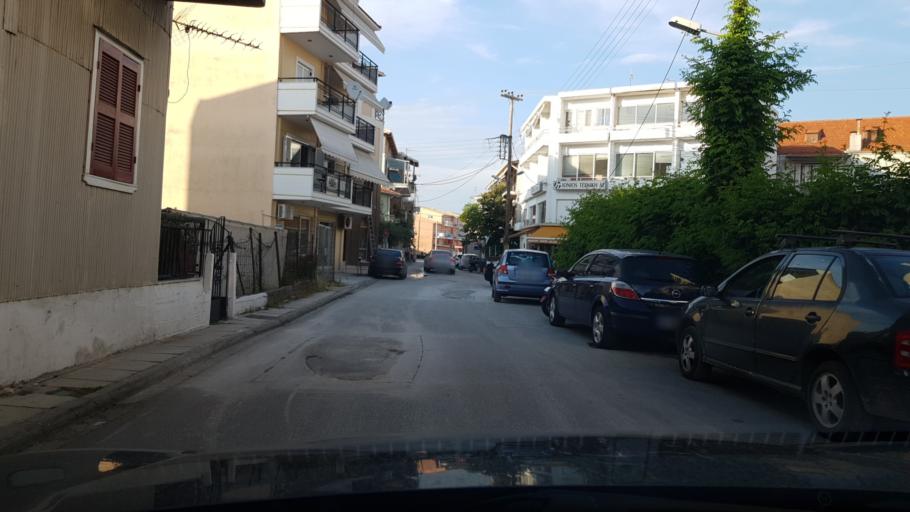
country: GR
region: Ionian Islands
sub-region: Lefkada
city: Lefkada
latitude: 38.8296
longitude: 20.7043
